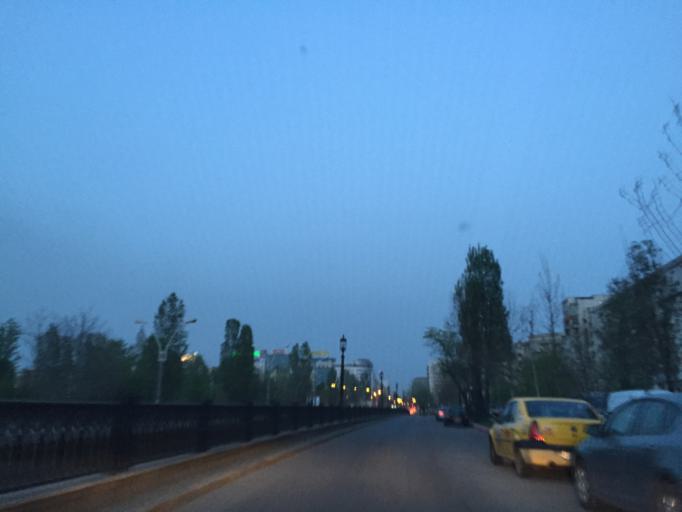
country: RO
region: Bucuresti
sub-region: Municipiul Bucuresti
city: Bucharest
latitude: 44.4237
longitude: 26.1134
